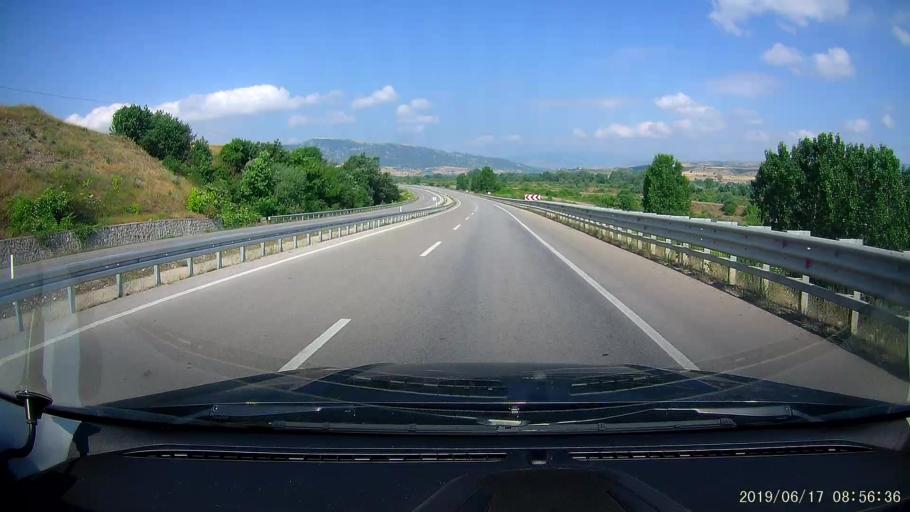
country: TR
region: Amasya
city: Esencay
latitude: 40.7347
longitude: 36.4173
